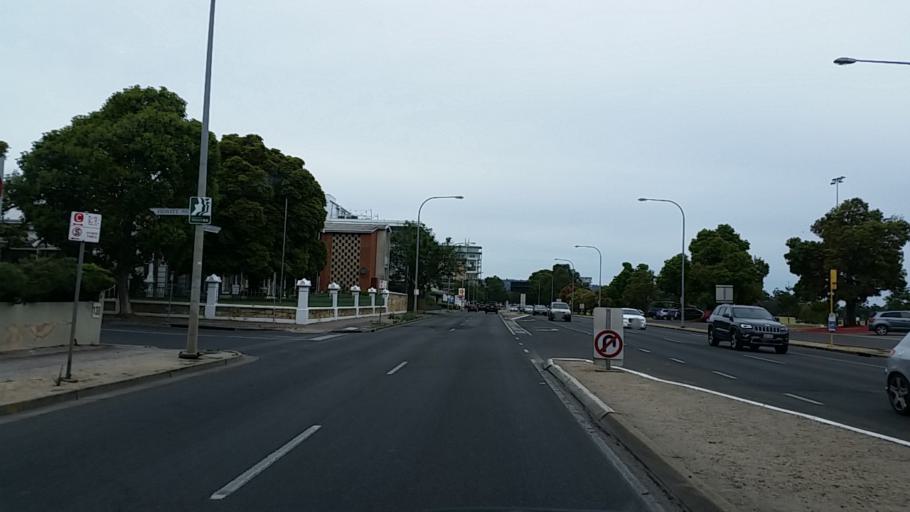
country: AU
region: South Australia
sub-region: Norwood Payneham St Peters
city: Trinity Gardens
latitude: -34.9287
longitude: 138.6237
